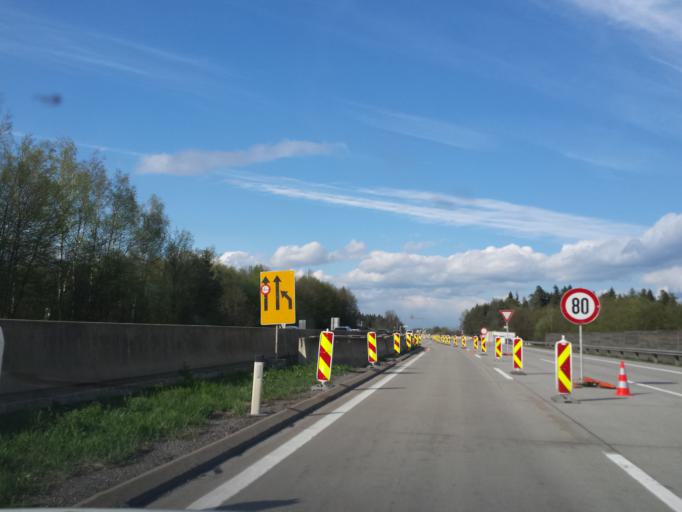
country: AT
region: Styria
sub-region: Politischer Bezirk Graz-Umgebung
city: Unterpremstatten
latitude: 46.9605
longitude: 15.3812
